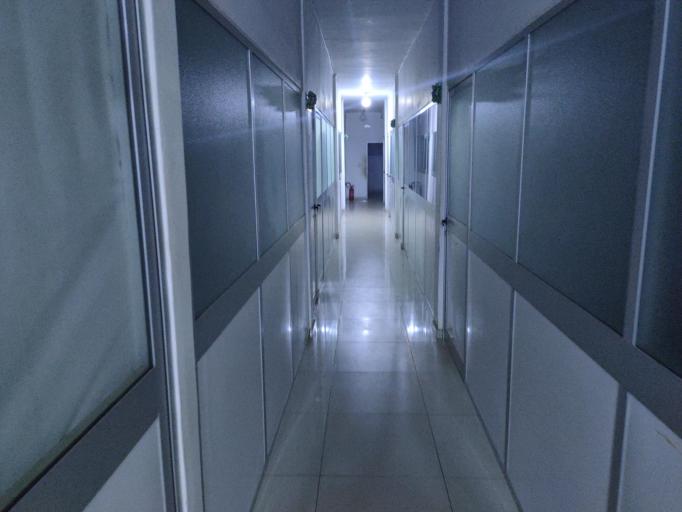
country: TG
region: Maritime
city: Lome
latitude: 6.1830
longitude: 1.1957
